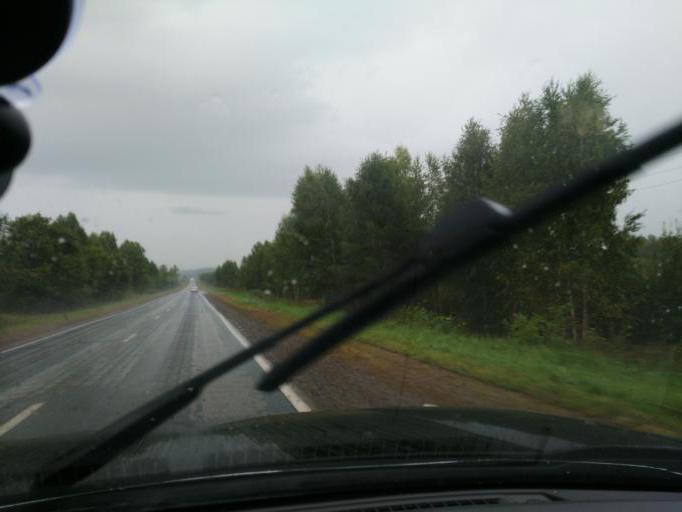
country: RU
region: Perm
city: Osa
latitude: 57.1304
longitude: 55.5256
